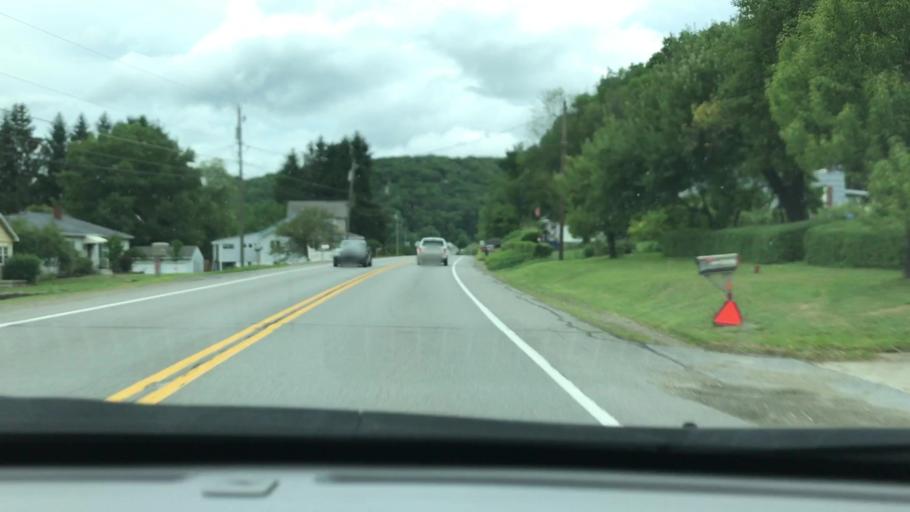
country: US
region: Pennsylvania
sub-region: Elk County
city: Johnsonburg
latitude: 41.4747
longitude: -78.6705
